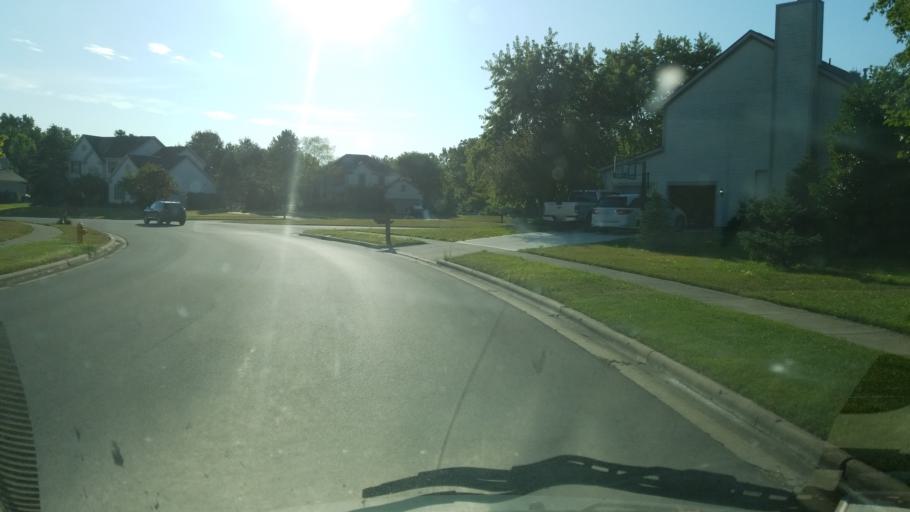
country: US
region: Ohio
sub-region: Delaware County
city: Lewis Center
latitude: 40.1720
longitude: -83.0015
